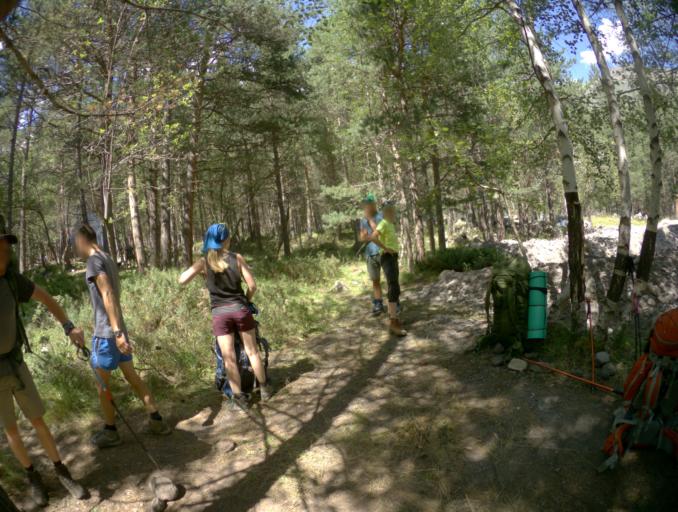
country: RU
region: Kabardino-Balkariya
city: Terskol
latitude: 43.2575
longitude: 42.5036
